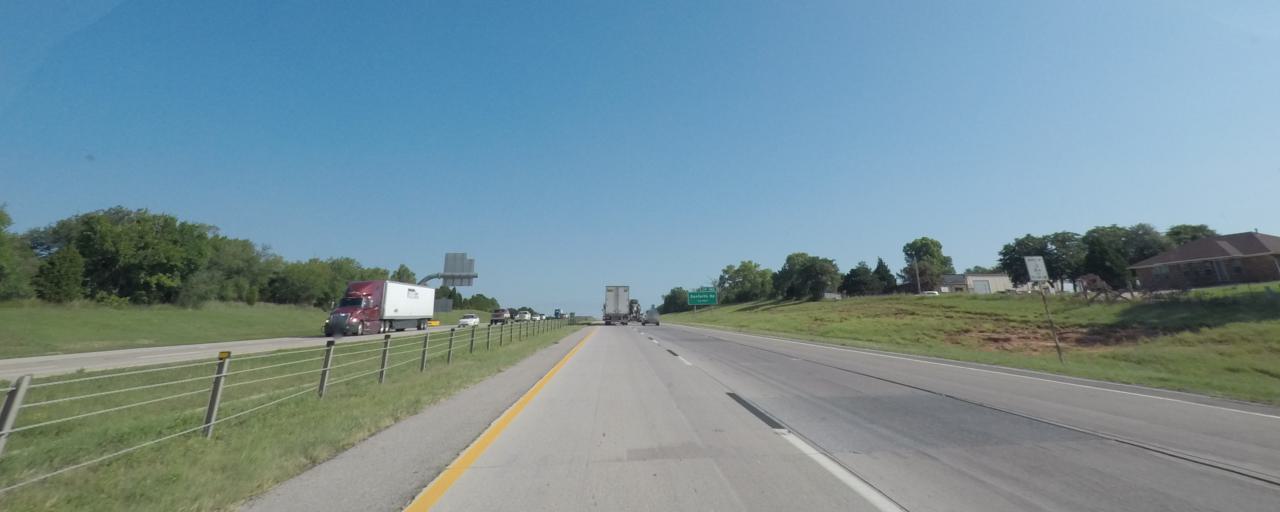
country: US
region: Oklahoma
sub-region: Oklahoma County
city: Edmond
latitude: 35.6562
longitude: -97.4236
